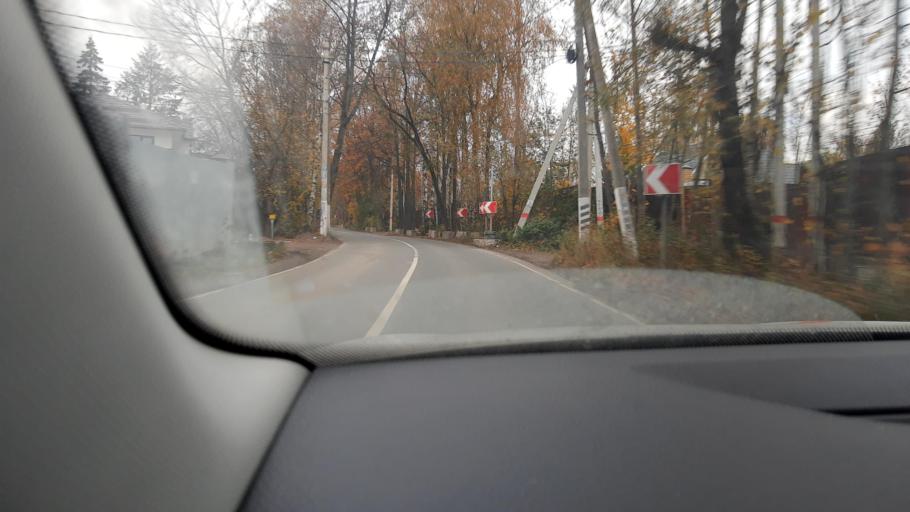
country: RU
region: Moscow
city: Annino
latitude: 55.5298
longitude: 37.6065
